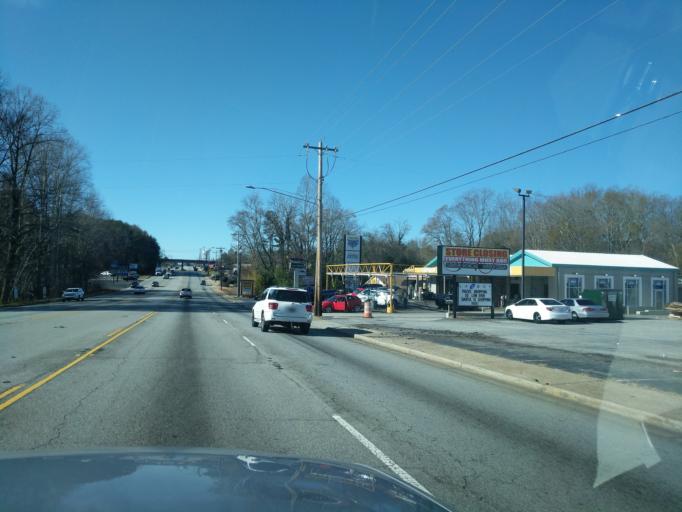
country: US
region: South Carolina
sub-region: Pickens County
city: Easley
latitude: 34.8233
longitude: -82.5806
